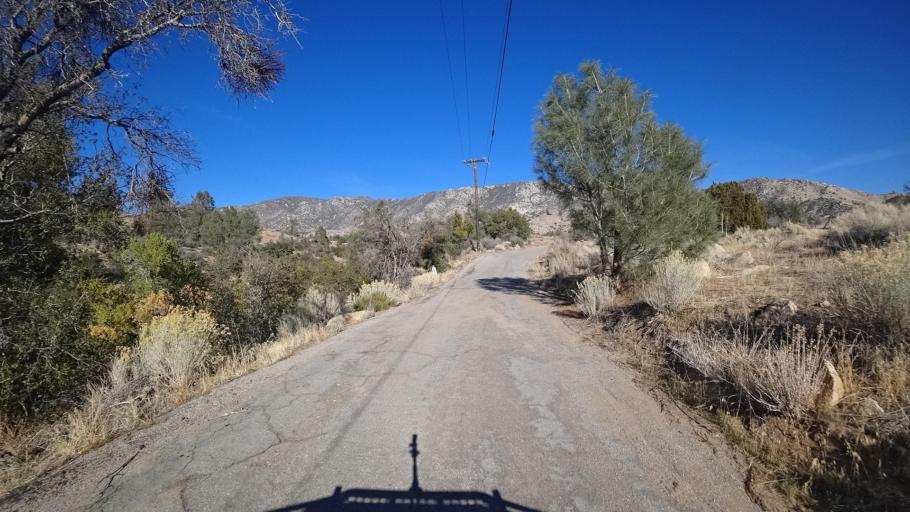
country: US
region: California
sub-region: Kern County
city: Weldon
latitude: 35.7235
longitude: -118.3058
